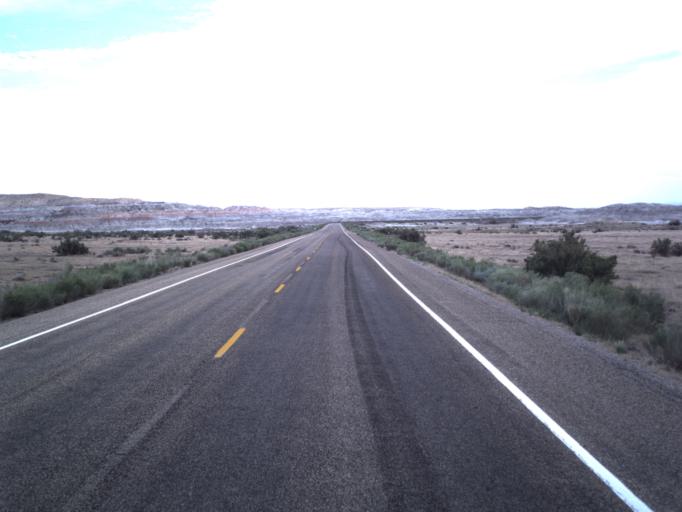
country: US
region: Utah
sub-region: Uintah County
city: Naples
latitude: 40.1122
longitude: -109.2360
